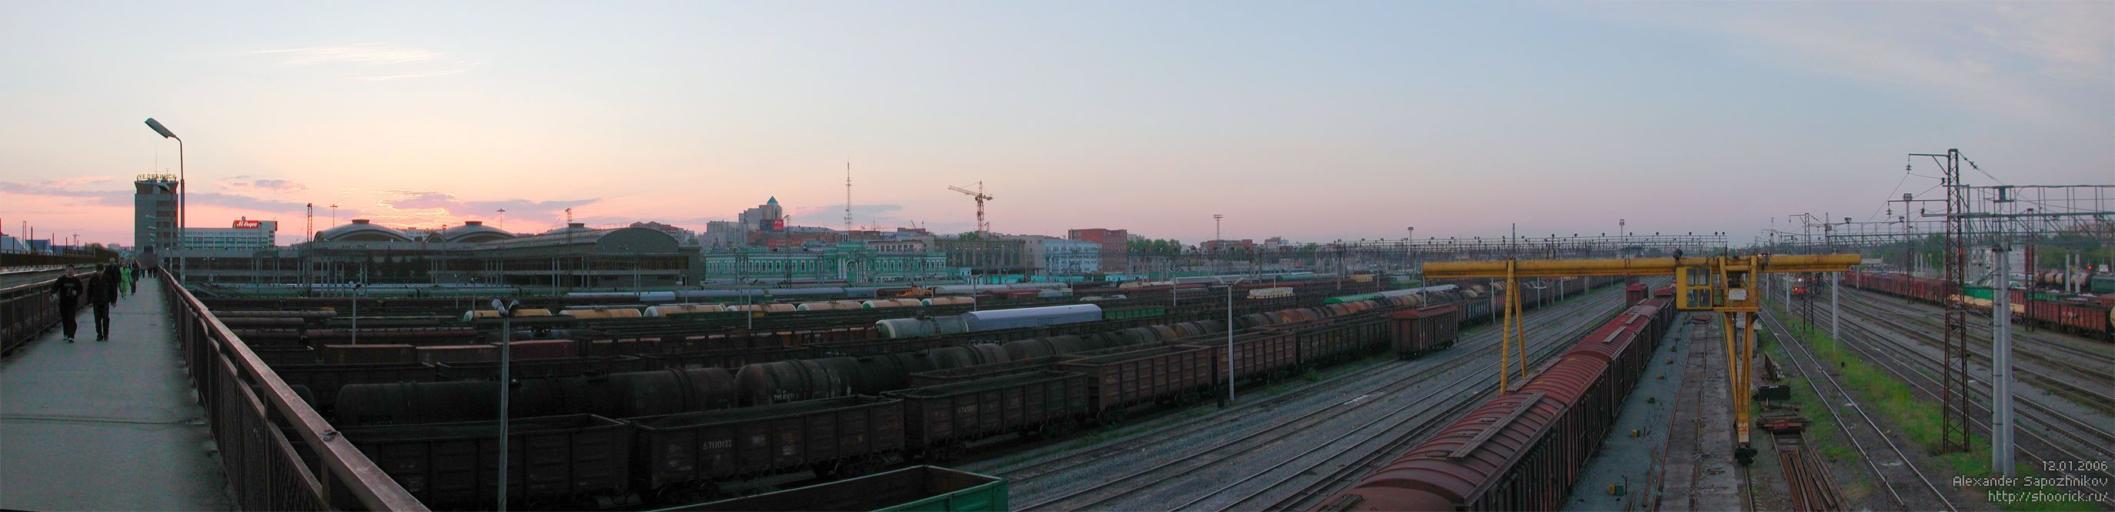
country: RU
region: Chelyabinsk
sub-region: Gorod Chelyabinsk
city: Chelyabinsk
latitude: 55.1396
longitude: 61.4198
